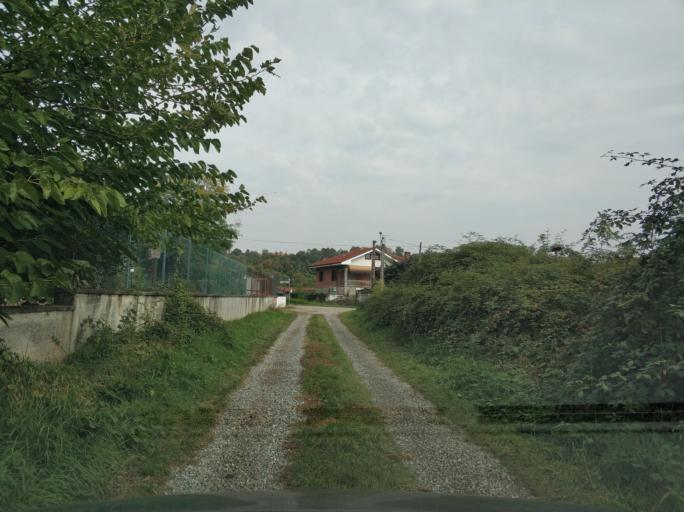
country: IT
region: Piedmont
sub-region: Provincia di Torino
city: Nole
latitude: 45.2547
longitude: 7.5706
